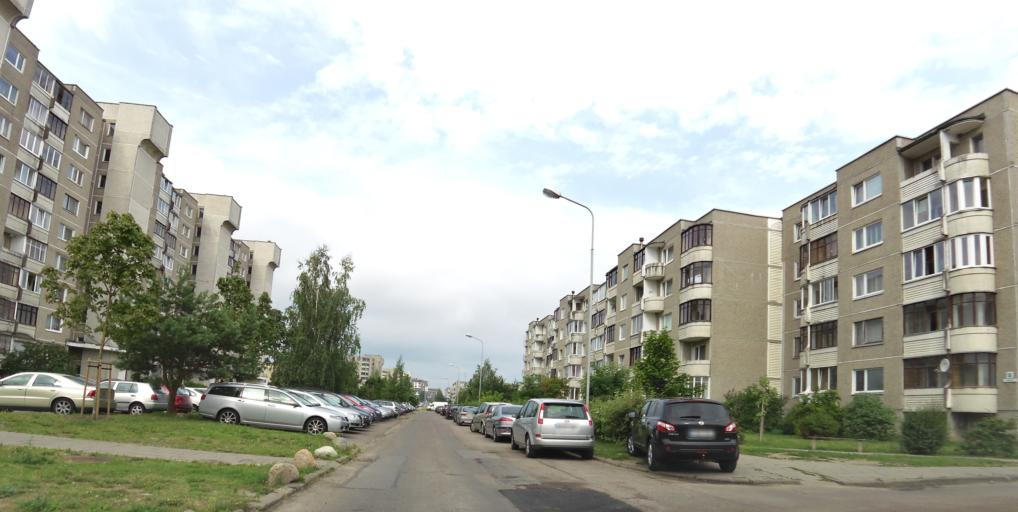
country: LT
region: Vilnius County
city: Pilaite
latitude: 54.7047
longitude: 25.1841
